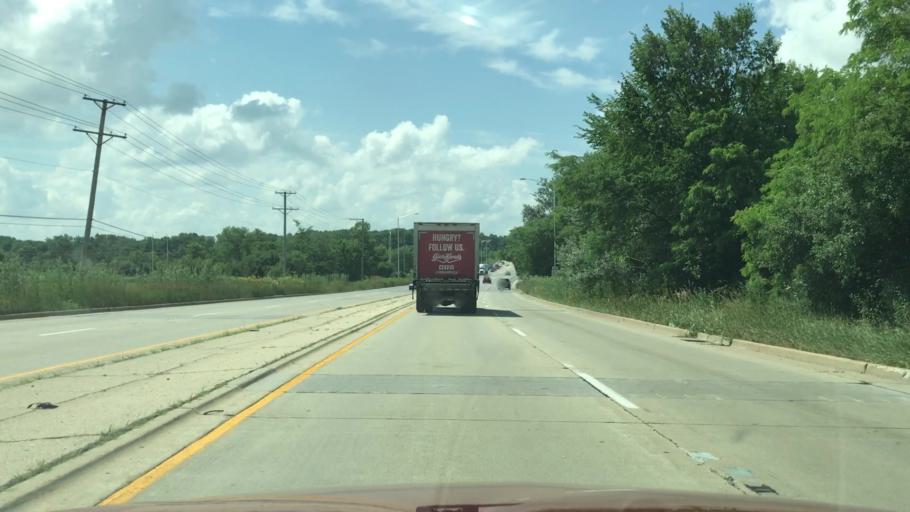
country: US
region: Illinois
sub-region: Cook County
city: Streamwood
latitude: 42.0480
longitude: -88.1936
